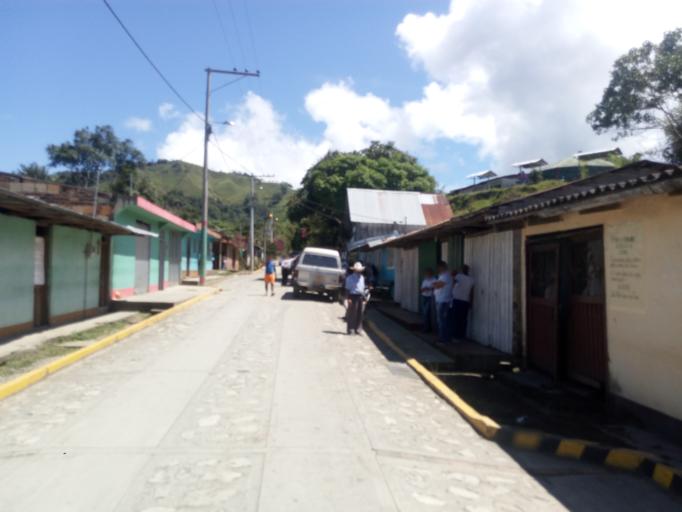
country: CO
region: Boyaca
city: Otanche
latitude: 5.5890
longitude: -74.2262
